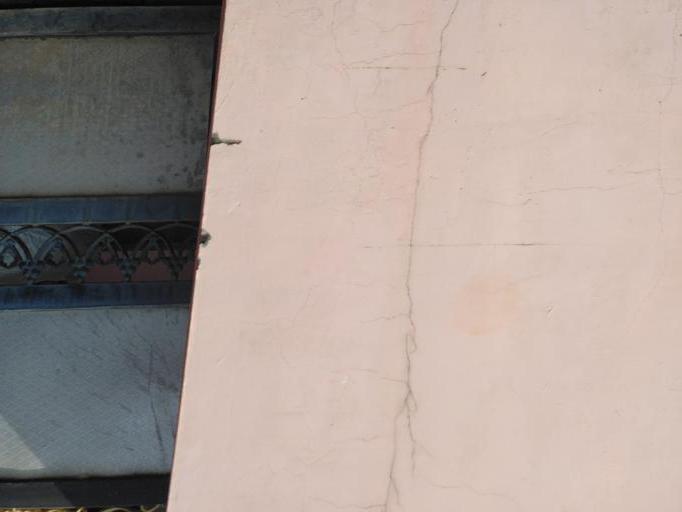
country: IN
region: Kerala
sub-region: Alappuzha
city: Arukutti
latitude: 9.9371
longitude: 76.3473
